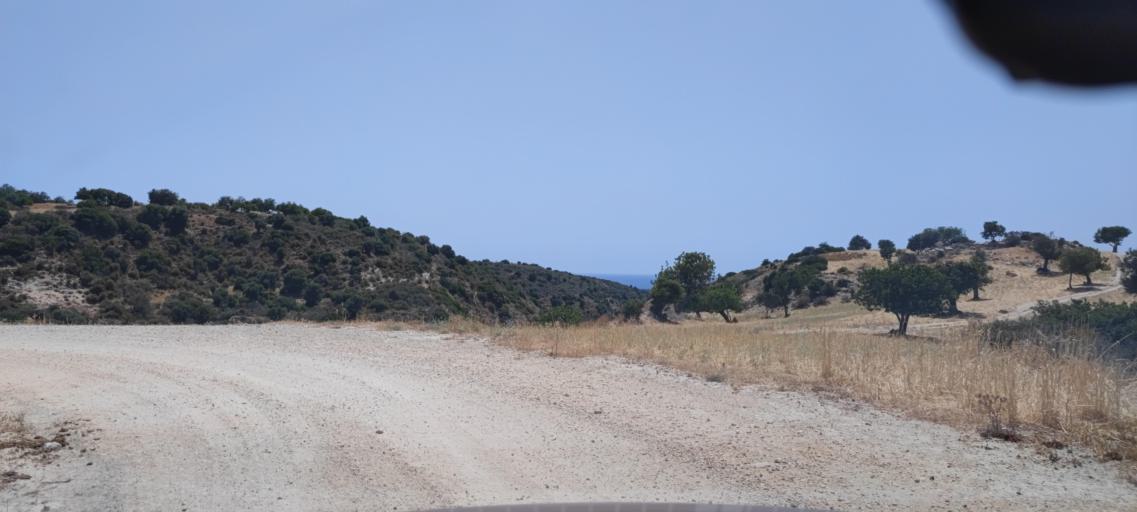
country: CY
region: Limassol
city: Pissouri
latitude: 34.7291
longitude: 32.5922
